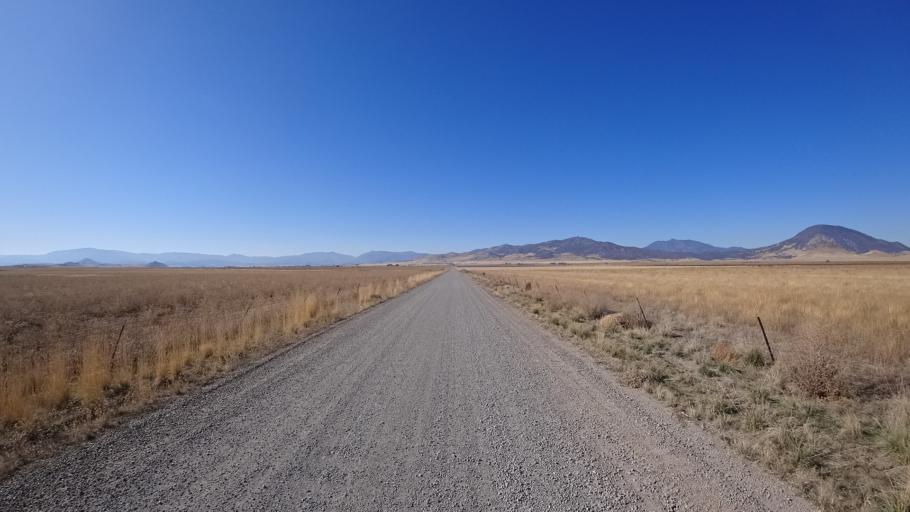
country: US
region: California
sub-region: Siskiyou County
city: Montague
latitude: 41.7865
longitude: -122.4381
